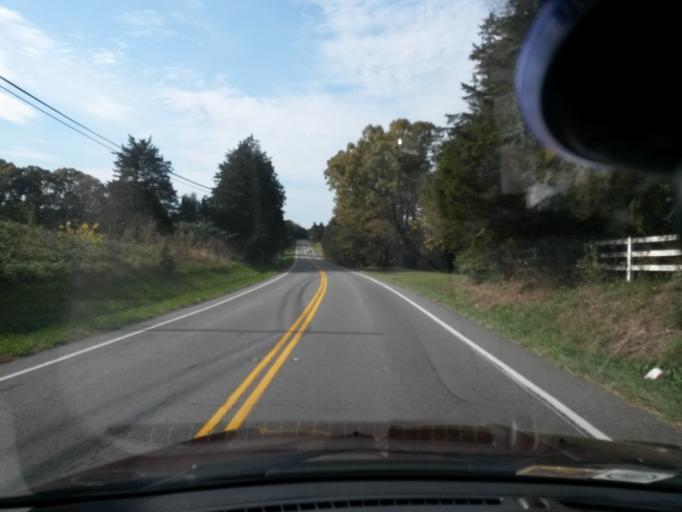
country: US
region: Virginia
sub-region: Franklin County
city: Rocky Mount
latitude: 37.1119
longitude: -79.8077
